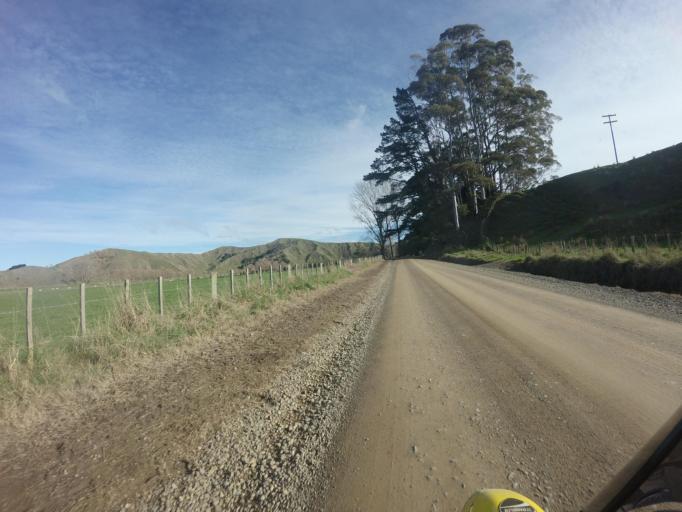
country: NZ
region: Hawke's Bay
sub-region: Wairoa District
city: Wairoa
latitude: -39.0256
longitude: 177.5769
